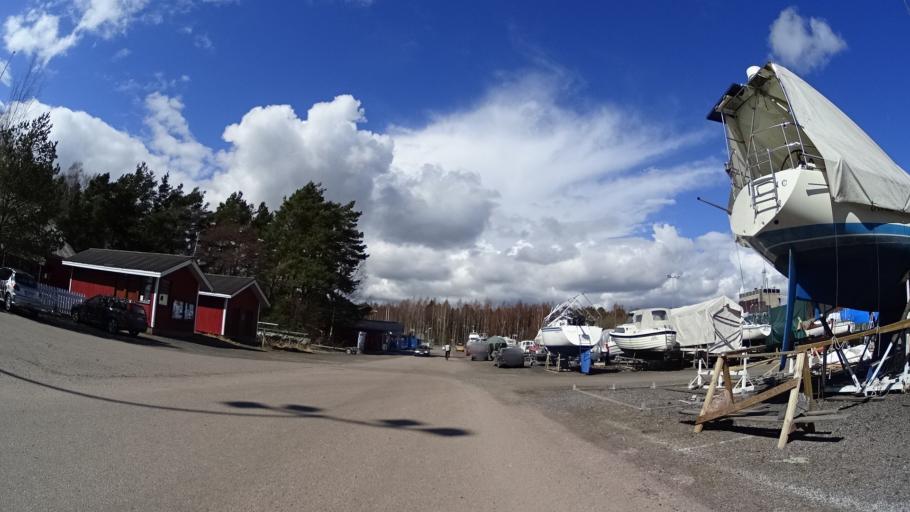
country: FI
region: Uusimaa
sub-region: Helsinki
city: Koukkuniemi
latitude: 60.1462
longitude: 24.7146
